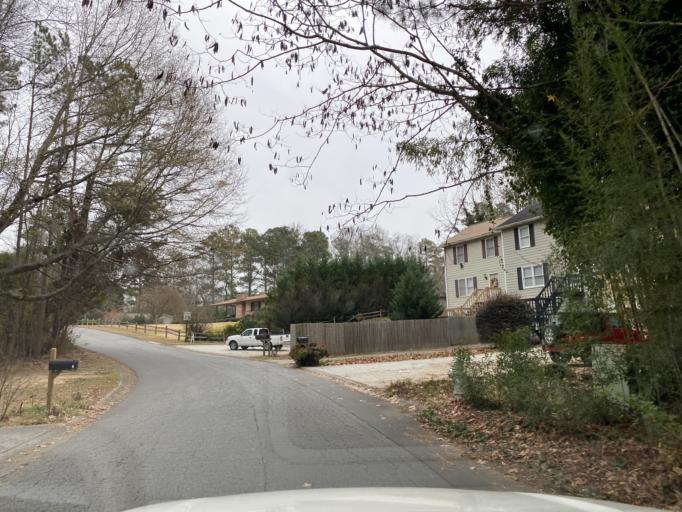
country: US
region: Georgia
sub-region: Cobb County
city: Fair Oaks
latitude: 33.9130
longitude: -84.5783
